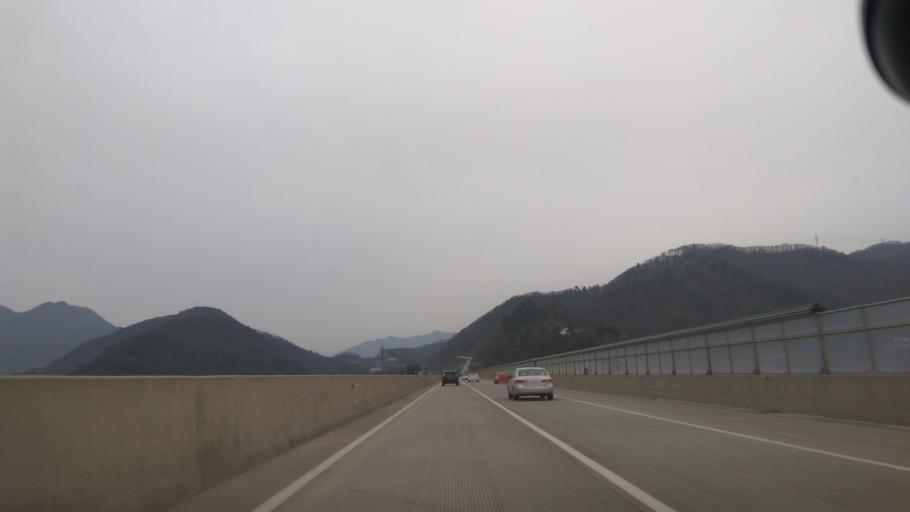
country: KR
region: Gyeonggi-do
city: Hwado
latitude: 37.6341
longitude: 127.3579
